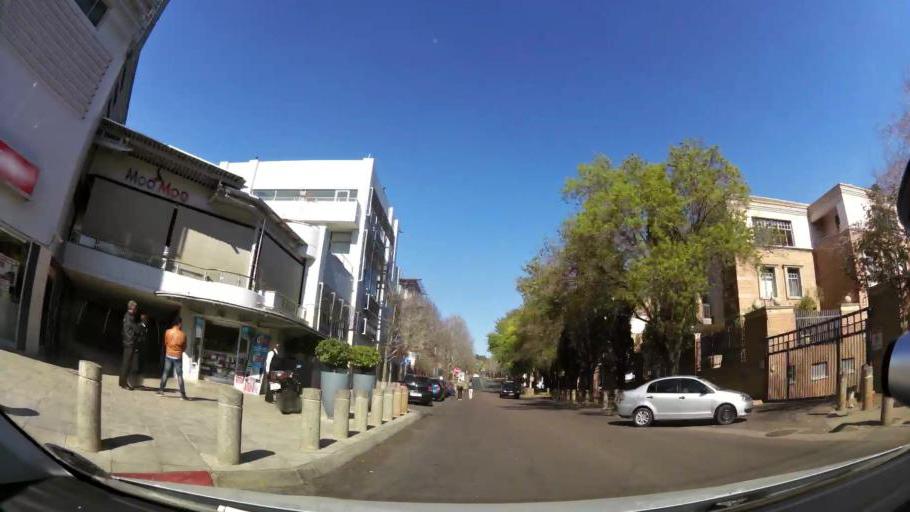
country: ZA
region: Gauteng
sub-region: City of Tshwane Metropolitan Municipality
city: Pretoria
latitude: -25.7716
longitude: 28.2328
